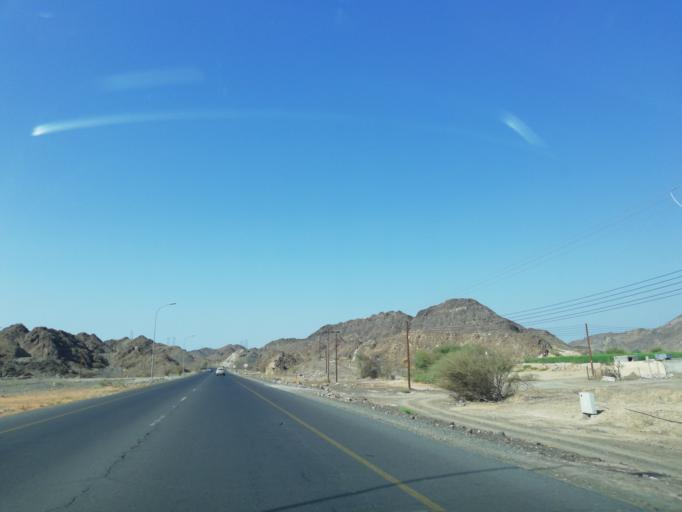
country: OM
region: Ash Sharqiyah
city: Ibra'
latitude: 22.8246
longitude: 58.1688
